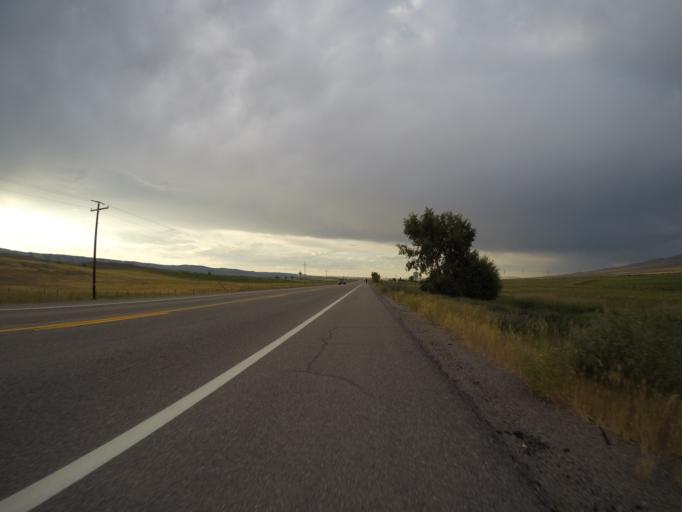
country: US
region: Idaho
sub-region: Bear Lake County
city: Montpelier
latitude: 42.0764
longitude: -110.9461
